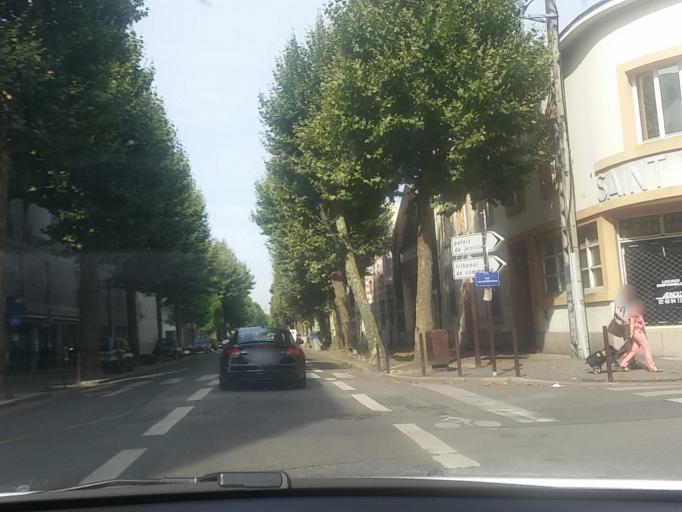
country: FR
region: Pays de la Loire
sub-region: Departement de la Loire-Atlantique
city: Nantes
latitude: 47.2053
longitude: -1.5563
